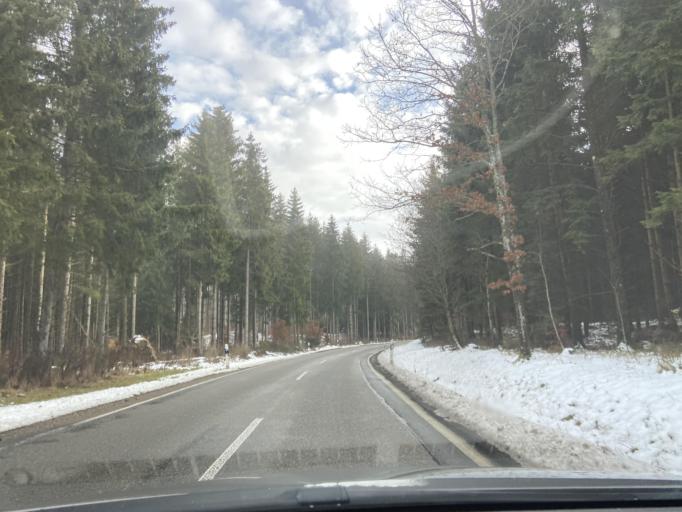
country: DE
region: Baden-Wuerttemberg
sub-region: Tuebingen Region
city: Pfronstetten
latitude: 48.2440
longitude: 9.3416
